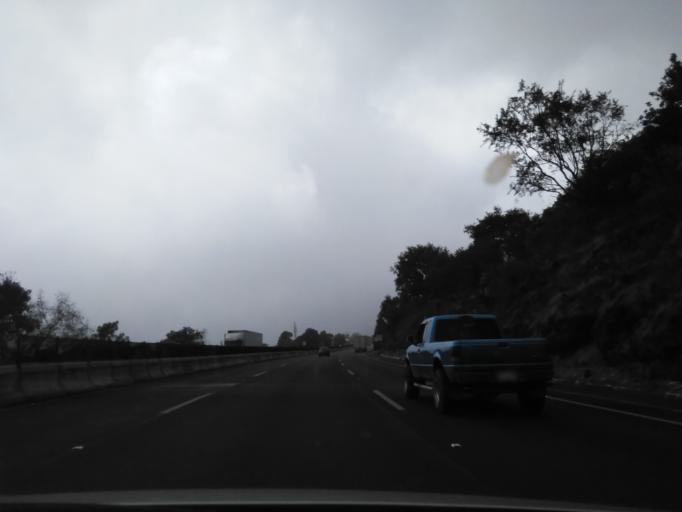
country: MX
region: Morelos
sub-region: Cuernavaca
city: Villa Santiago
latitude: 19.0251
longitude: -99.1884
